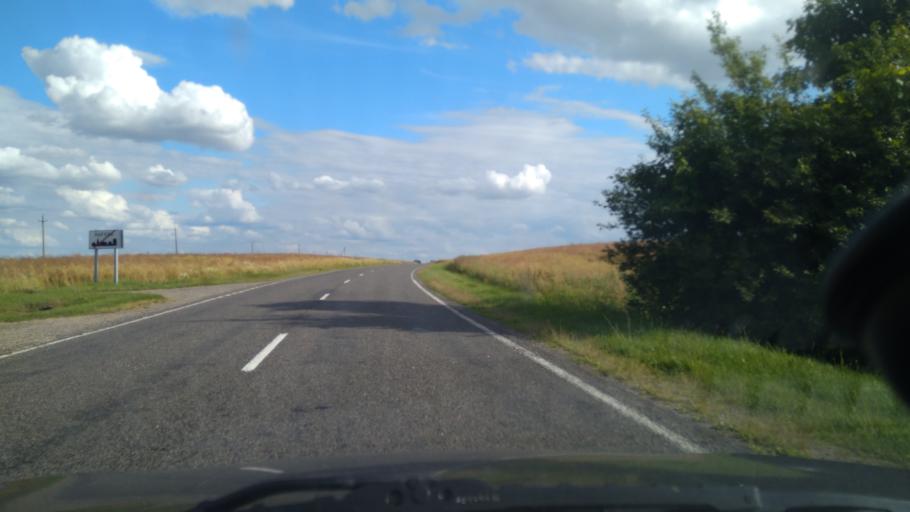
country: BY
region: Grodnenskaya
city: Masty
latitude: 53.3384
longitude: 24.6712
